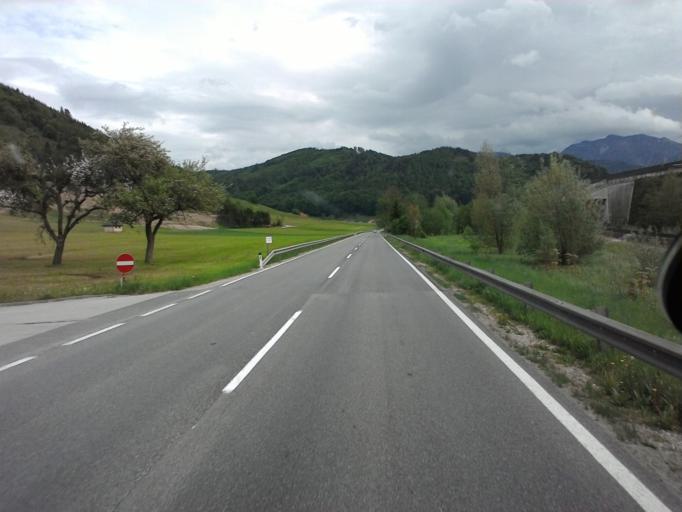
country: AT
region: Upper Austria
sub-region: Politischer Bezirk Kirchdorf an der Krems
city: Micheldorf in Oberoesterreich
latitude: 47.8675
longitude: 14.1445
